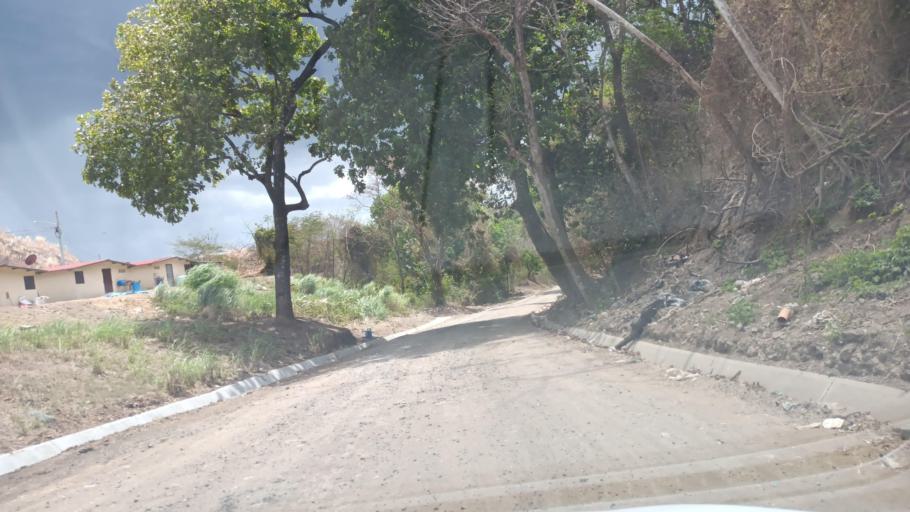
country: PA
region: Panama
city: Las Cumbres
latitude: 9.0626
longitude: -79.5661
